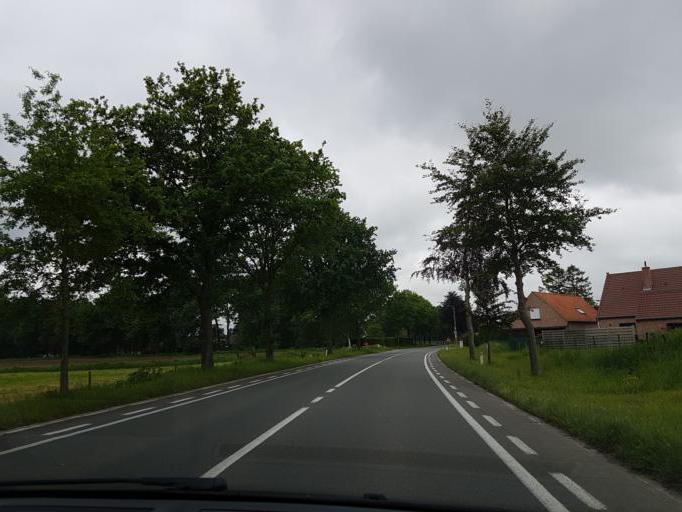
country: BE
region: Flanders
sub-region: Provincie West-Vlaanderen
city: Beernem
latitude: 51.1231
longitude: 3.3639
